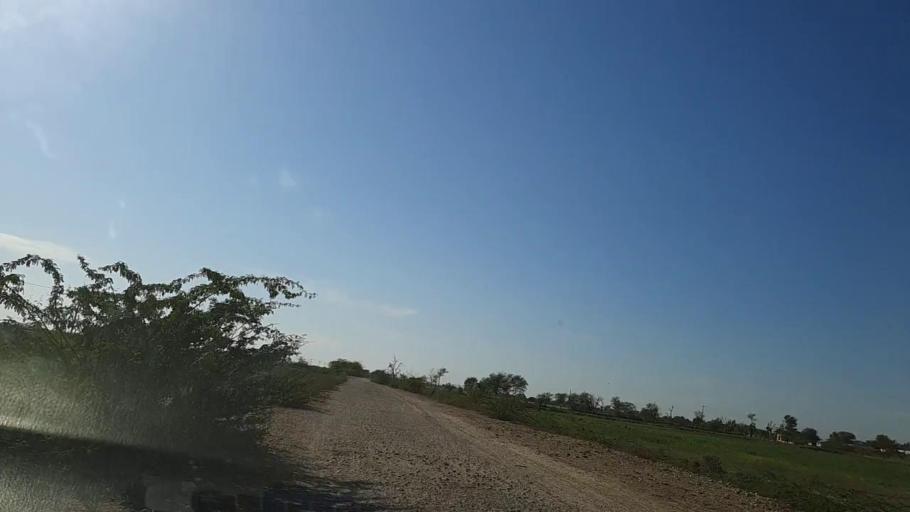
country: PK
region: Sindh
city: Dhoro Naro
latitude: 25.5046
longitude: 69.5328
